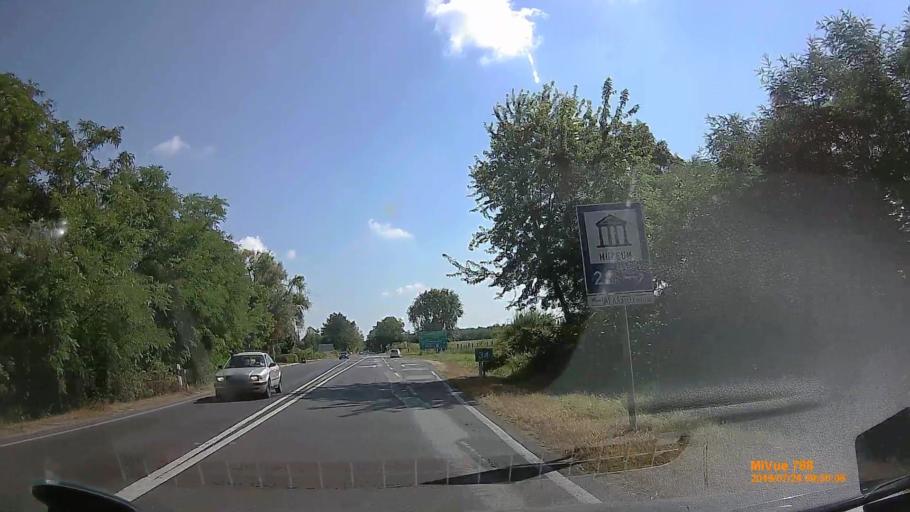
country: HU
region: Szabolcs-Szatmar-Bereg
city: Vaja
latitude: 48.0188
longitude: 22.1456
